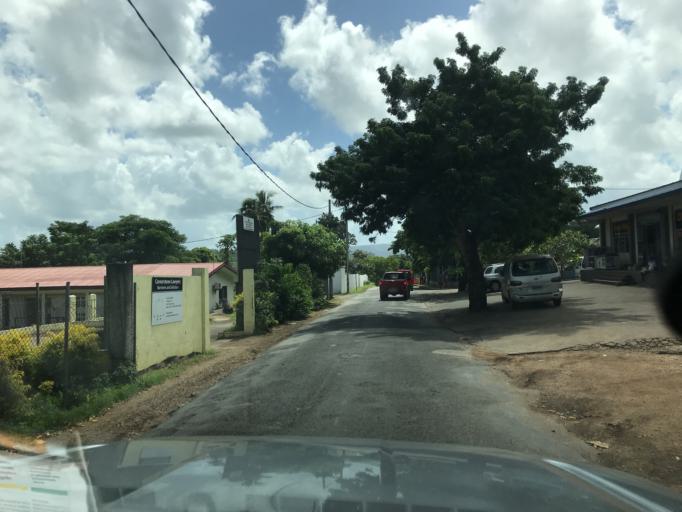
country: VU
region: Shefa
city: Port-Vila
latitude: -17.7335
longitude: 168.3124
